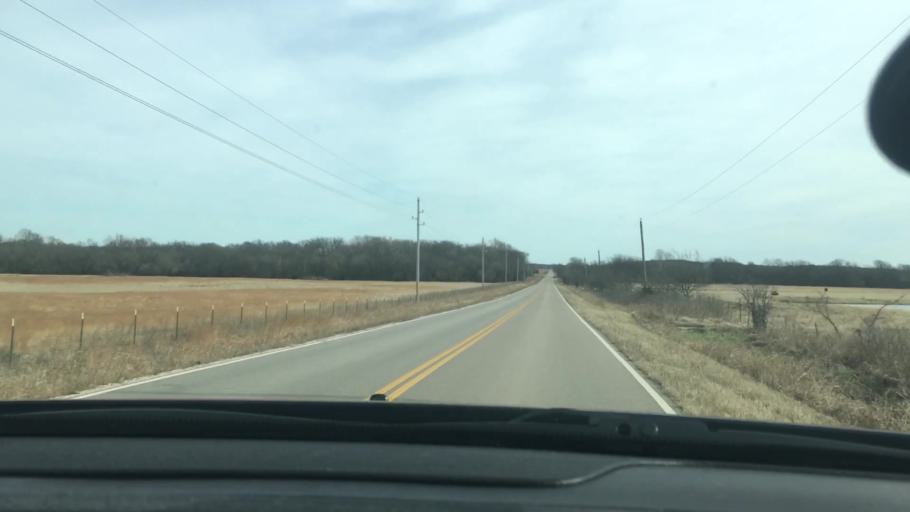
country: US
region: Oklahoma
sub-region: Murray County
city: Sulphur
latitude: 34.4031
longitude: -96.8698
